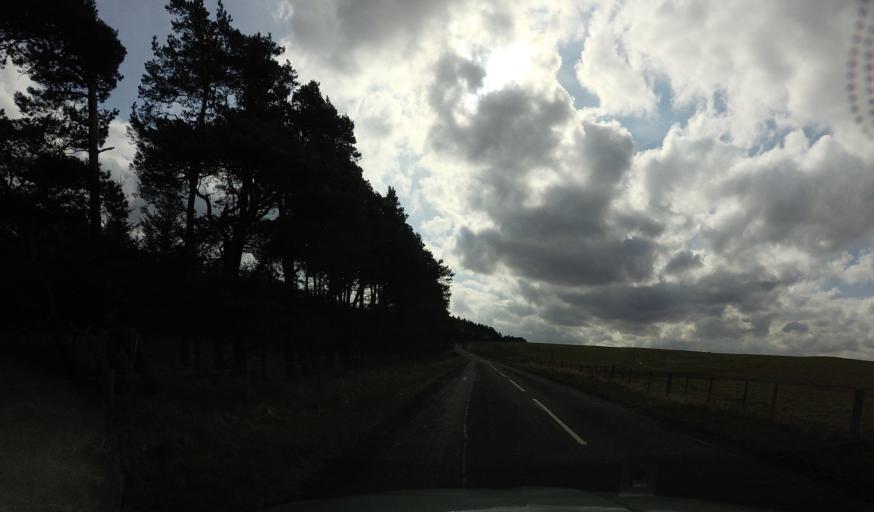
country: GB
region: Scotland
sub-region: Midlothian
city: Loanhead
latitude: 55.7941
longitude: -3.1427
